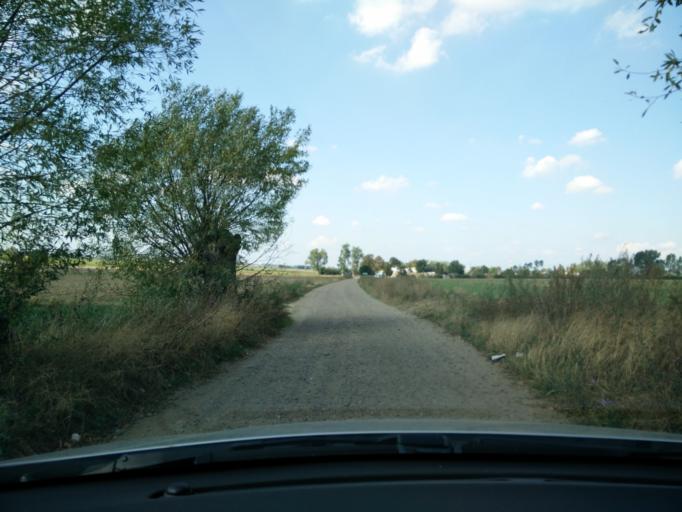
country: PL
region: Greater Poland Voivodeship
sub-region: Powiat poznanski
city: Kleszczewo
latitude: 52.2643
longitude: 17.1780
